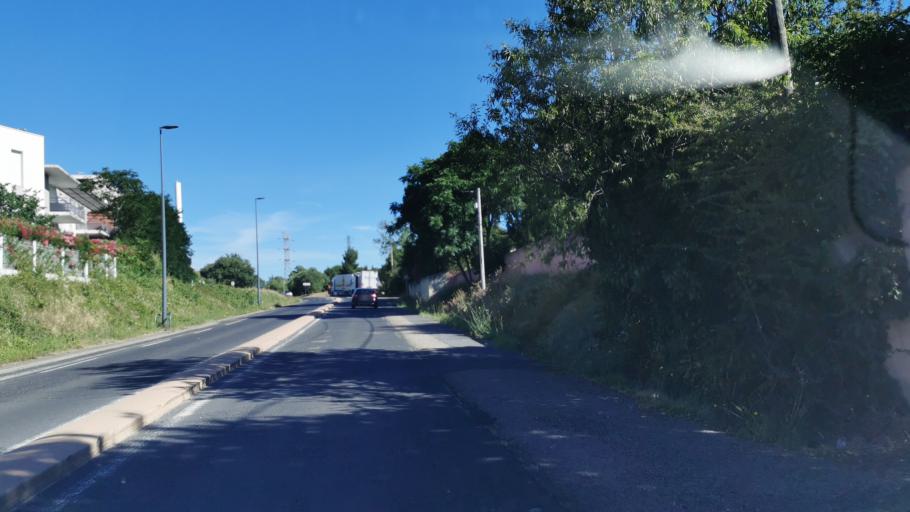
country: FR
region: Languedoc-Roussillon
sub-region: Departement de l'Herault
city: Beziers
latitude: 43.3639
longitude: 3.2116
